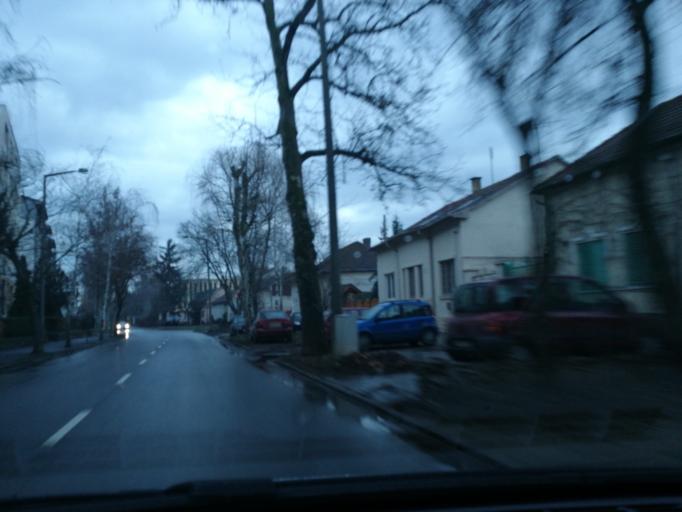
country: HU
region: Szabolcs-Szatmar-Bereg
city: Nyiregyhaza
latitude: 47.9460
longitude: 21.7151
